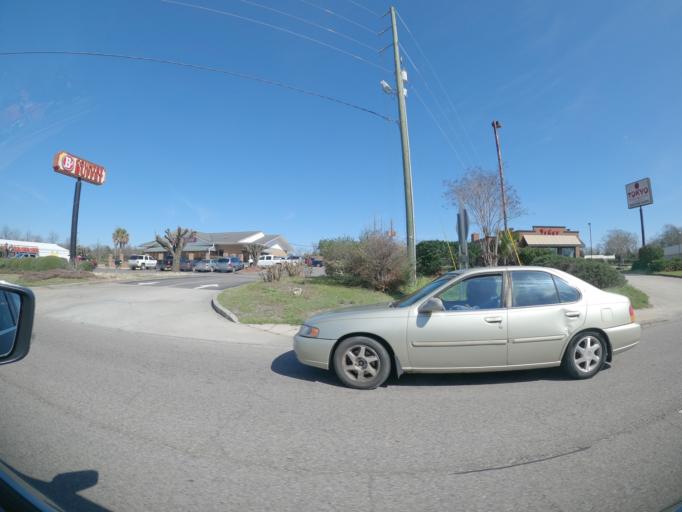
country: US
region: South Carolina
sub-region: Aiken County
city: North Augusta
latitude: 33.4904
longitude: -81.9521
